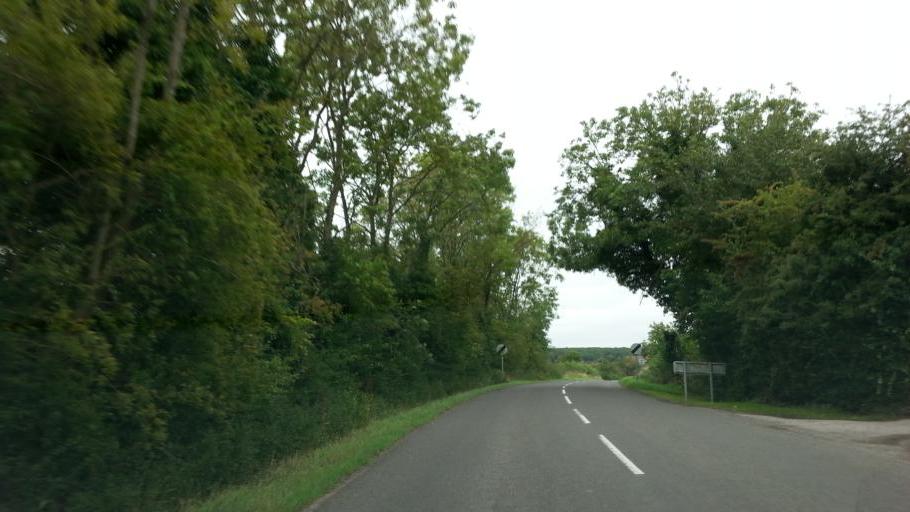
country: GB
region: England
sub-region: Nottinghamshire
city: Southwell
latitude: 53.1028
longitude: -0.9306
